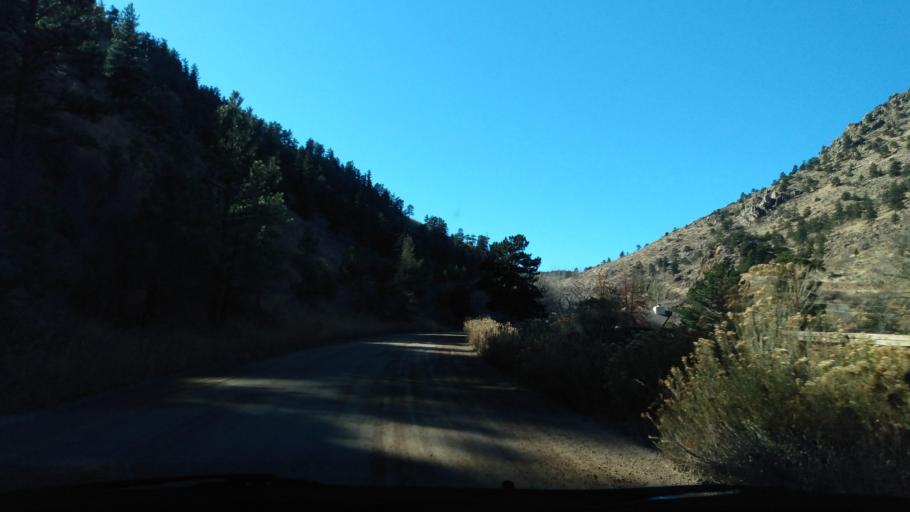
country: US
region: Colorado
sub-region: Boulder County
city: Lyons
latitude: 40.2399
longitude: -105.3130
